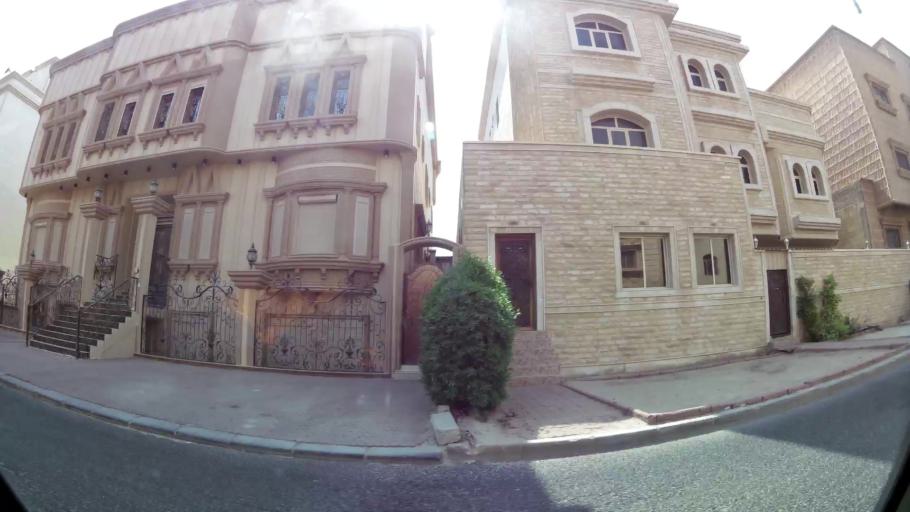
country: KW
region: Muhafazat al Jahra'
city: Al Jahra'
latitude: 29.3049
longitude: 47.6912
